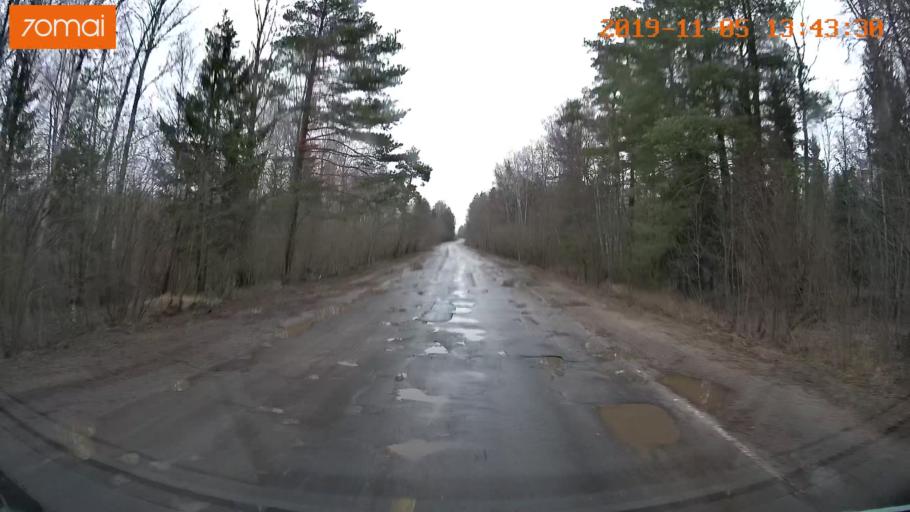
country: RU
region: Ivanovo
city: Shuya
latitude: 56.9739
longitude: 41.4034
